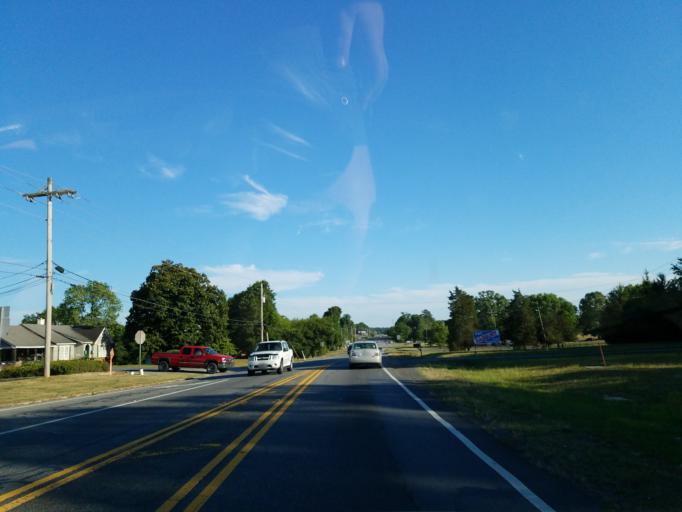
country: US
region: Georgia
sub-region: Gordon County
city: Calhoun
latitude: 34.4771
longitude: -84.9345
